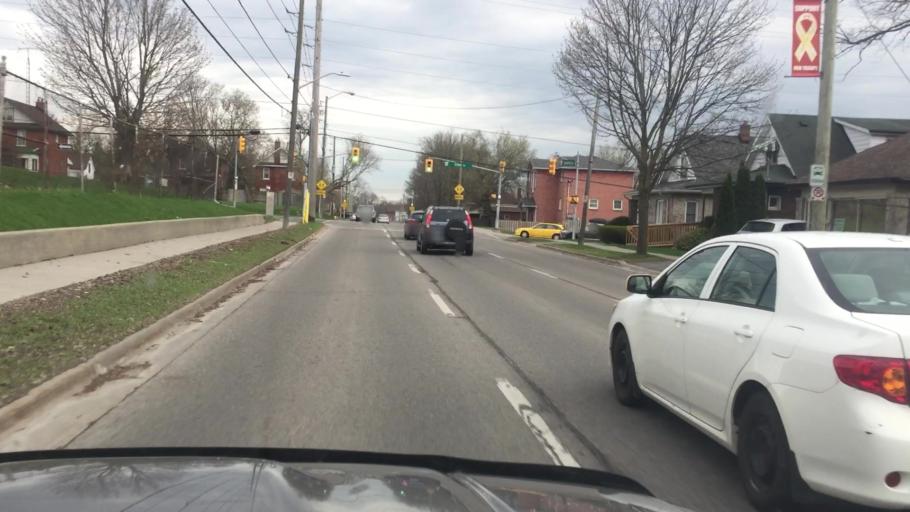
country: CA
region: Ontario
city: Oshawa
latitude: 43.8906
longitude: -78.8625
